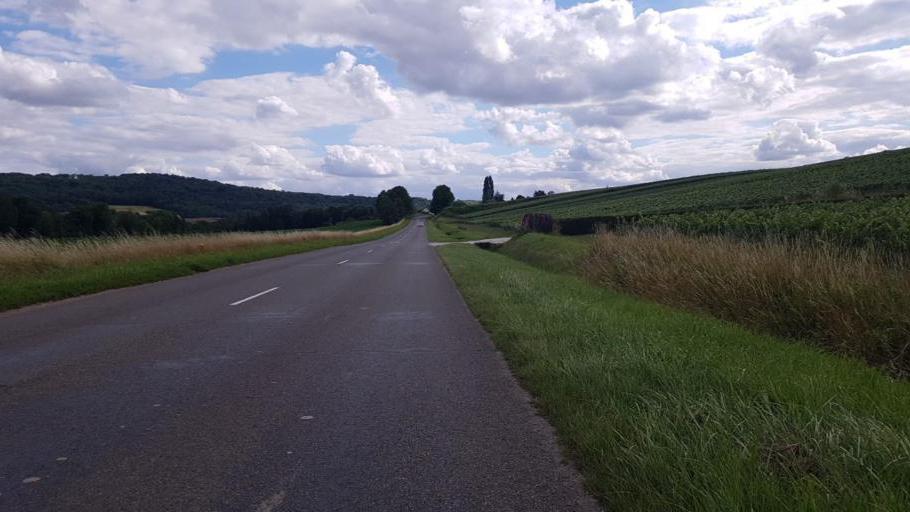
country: FR
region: Picardie
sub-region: Departement de l'Aisne
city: Crezancy
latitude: 49.0572
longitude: 3.4741
